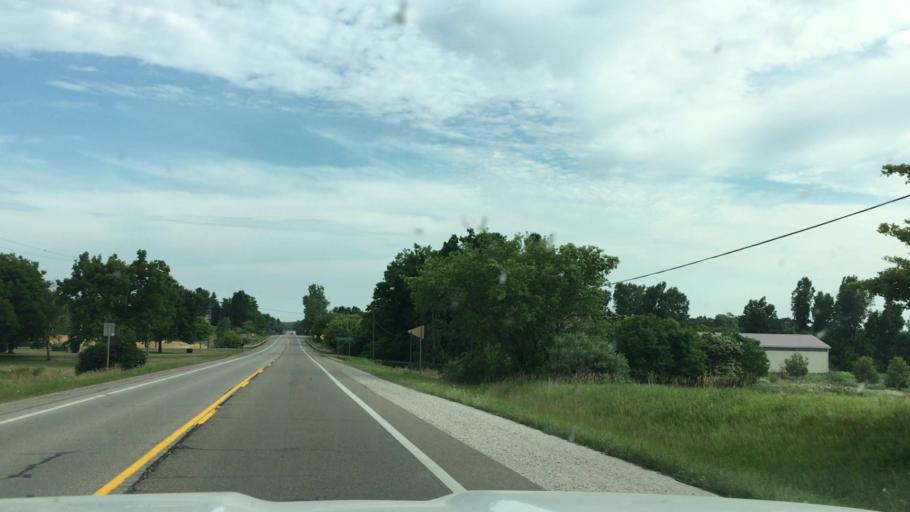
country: US
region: Michigan
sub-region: Sanilac County
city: Brown City
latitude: 43.1849
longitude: -83.0765
